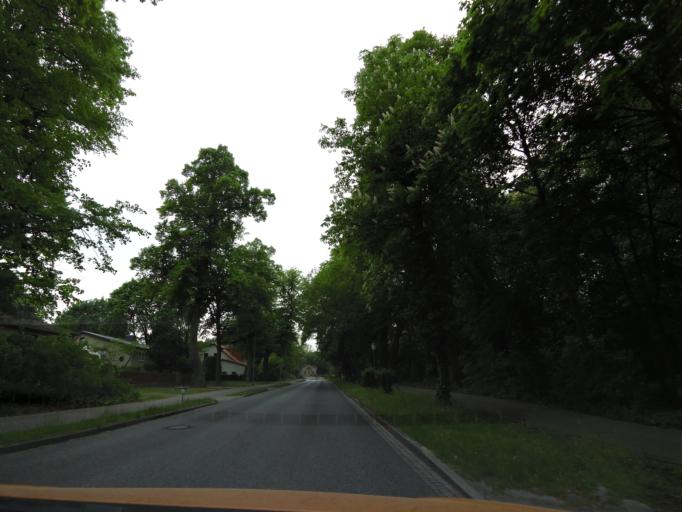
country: DE
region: Brandenburg
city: Kleinmachnow
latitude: 52.3958
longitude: 13.2251
